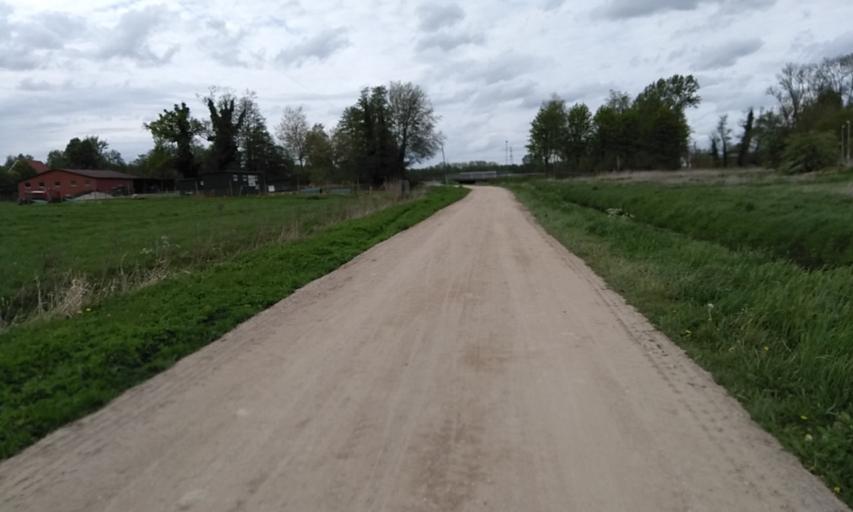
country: DE
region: Lower Saxony
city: Buxtehude
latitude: 53.4823
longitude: 9.6828
